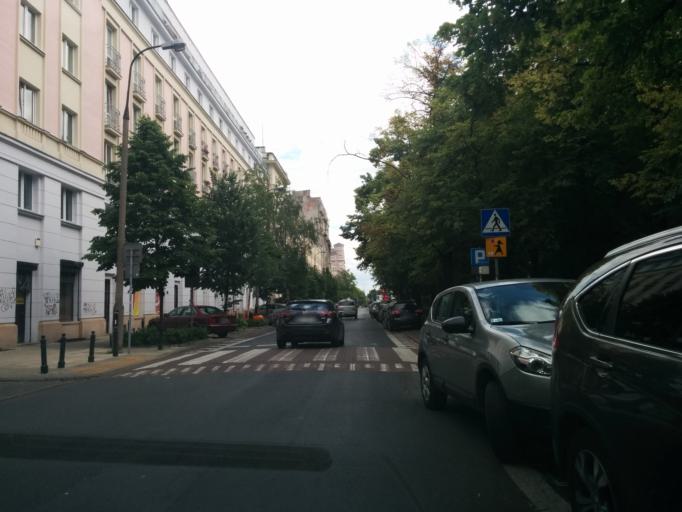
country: PL
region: Masovian Voivodeship
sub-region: Warszawa
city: Srodmiescie
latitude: 52.2155
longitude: 21.0186
